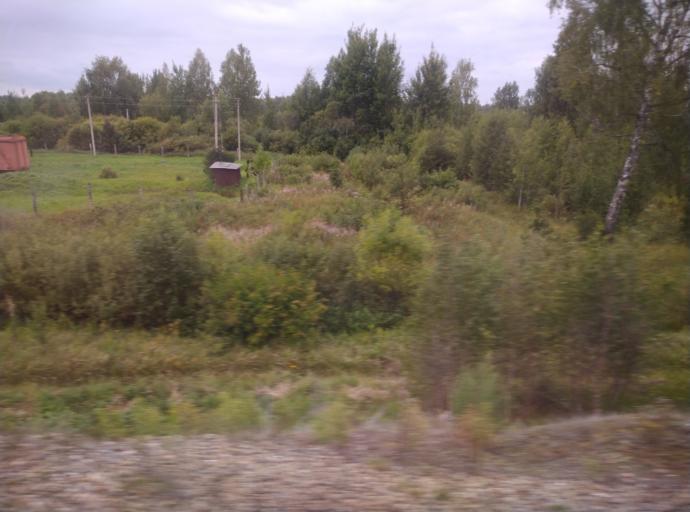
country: RU
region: Kostroma
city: Kosmynino
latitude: 57.5933
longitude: 40.7698
